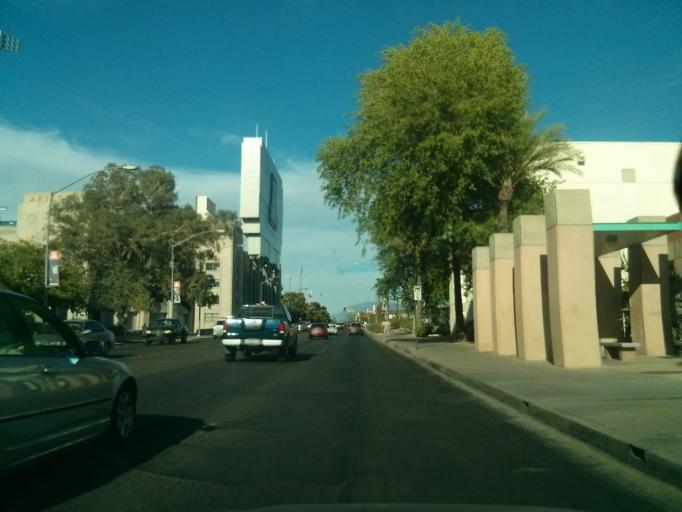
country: US
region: Arizona
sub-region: Pima County
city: Tucson
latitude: 32.2278
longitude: -110.9504
